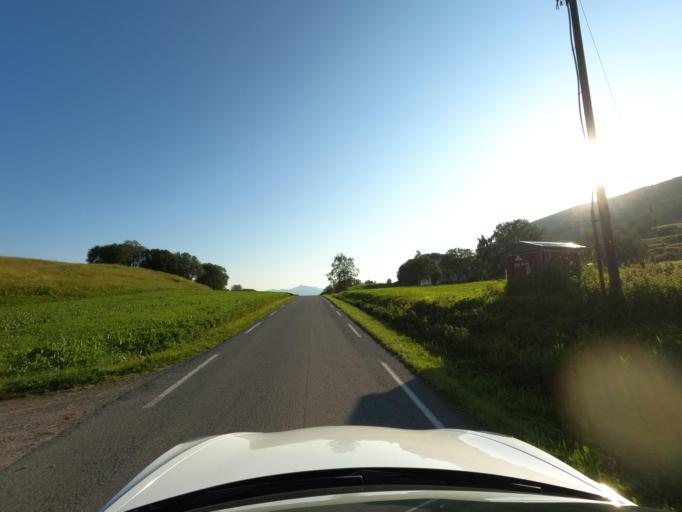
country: NO
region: Nordland
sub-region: Evenes
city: Randa
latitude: 68.4716
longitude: 16.8709
